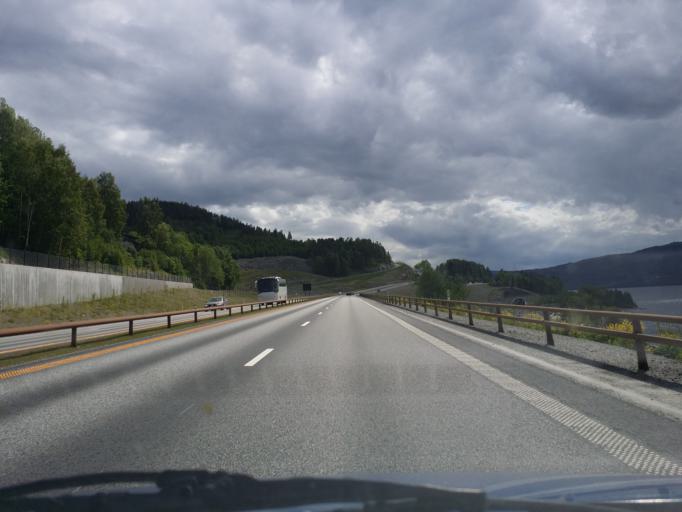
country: NO
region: Akershus
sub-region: Eidsvoll
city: Eidsvoll
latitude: 60.5097
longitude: 11.2429
